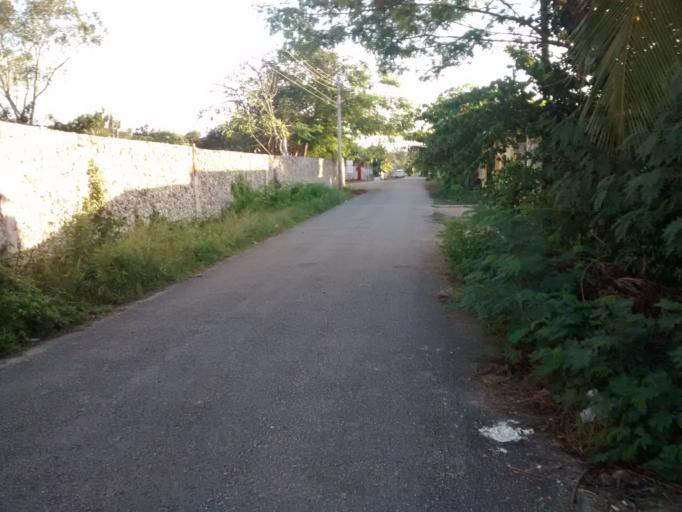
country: MX
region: Yucatan
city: Valladolid
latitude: 20.6833
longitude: -88.1863
